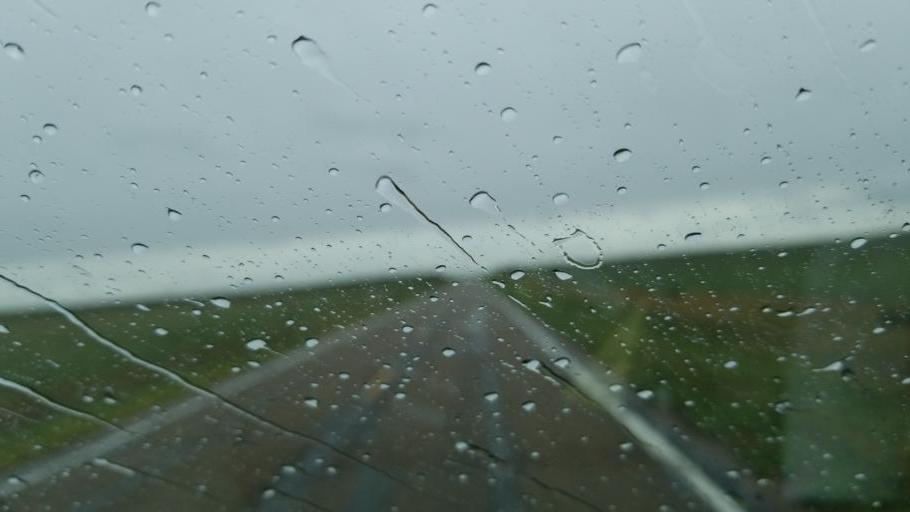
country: US
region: Colorado
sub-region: Lincoln County
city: Hugo
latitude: 38.8498
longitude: -103.1964
